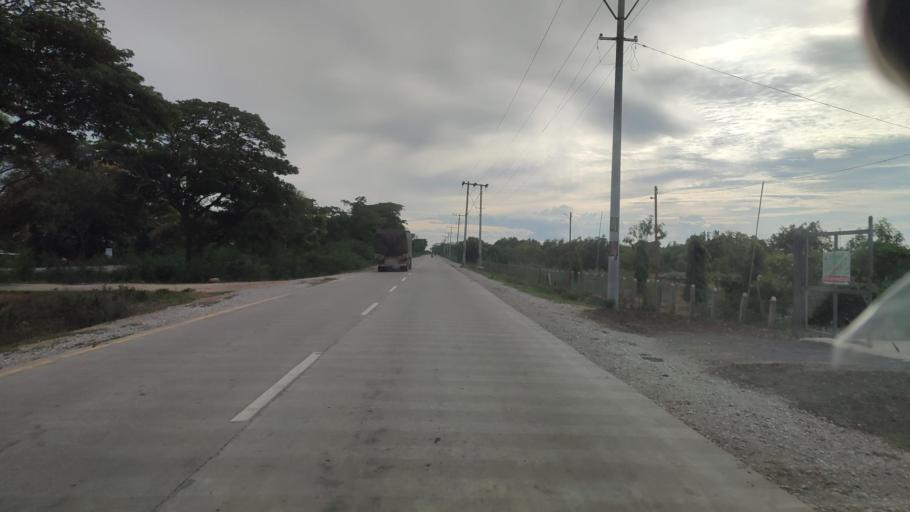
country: MM
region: Mandalay
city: Kyaukse
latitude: 21.3439
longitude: 96.0821
